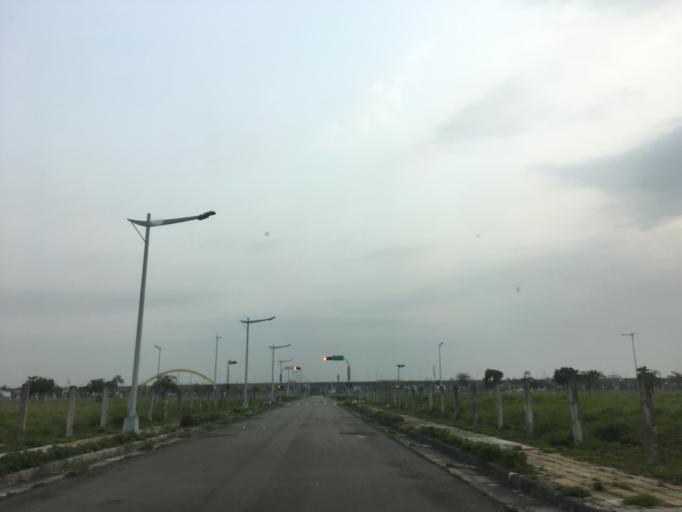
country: TW
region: Taiwan
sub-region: Taichung City
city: Taichung
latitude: 24.1960
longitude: 120.6722
